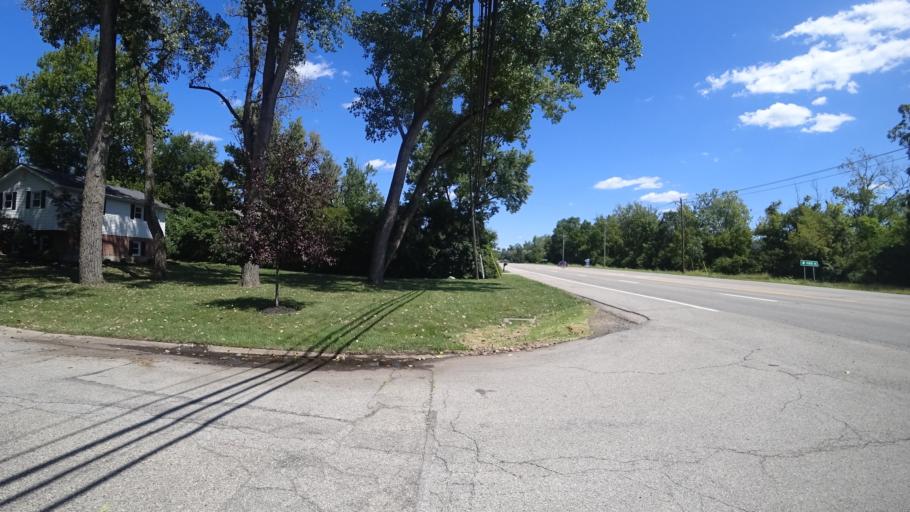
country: US
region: Ohio
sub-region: Butler County
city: New Miami
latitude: 39.4043
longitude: -84.5287
